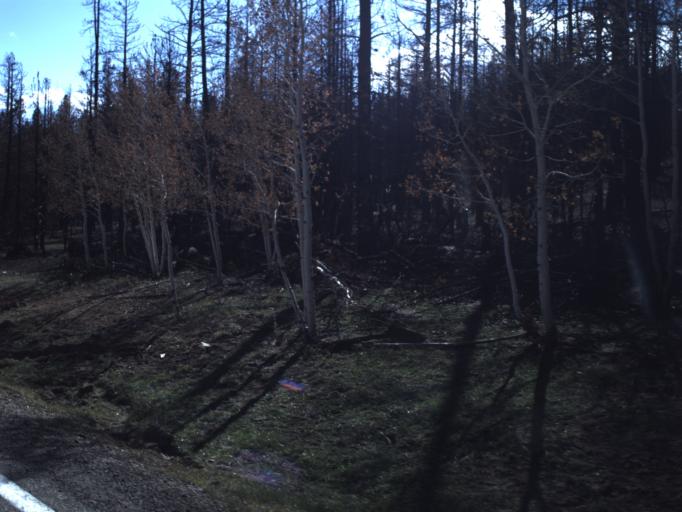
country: US
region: Utah
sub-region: Iron County
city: Parowan
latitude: 37.6612
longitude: -112.6657
